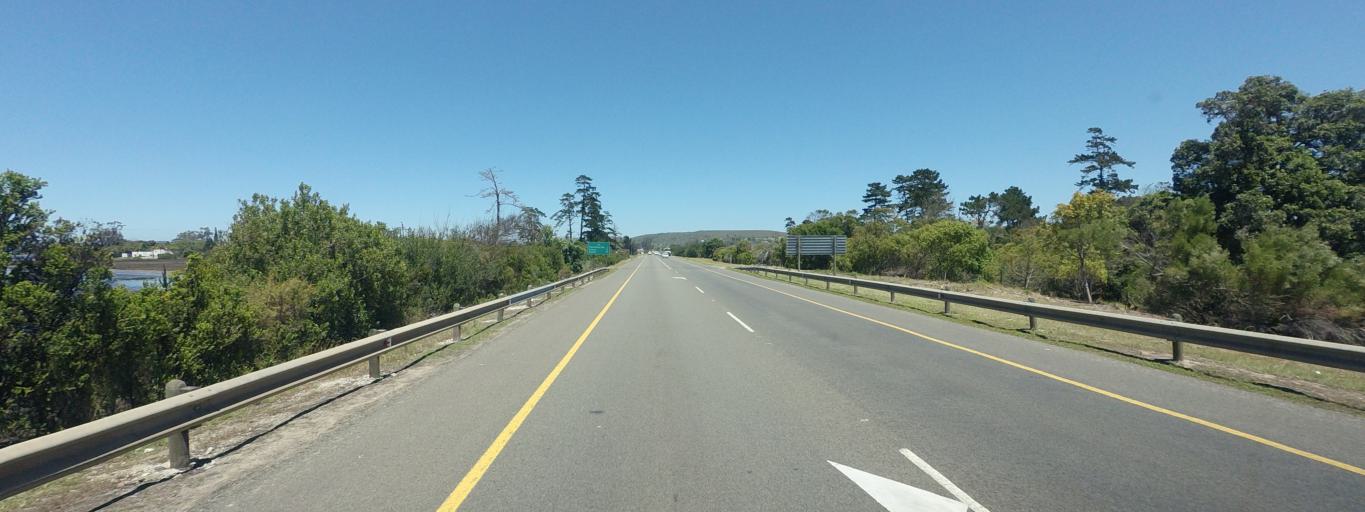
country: ZA
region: Western Cape
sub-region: Eden District Municipality
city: Plettenberg Bay
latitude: -34.0101
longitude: 23.3911
